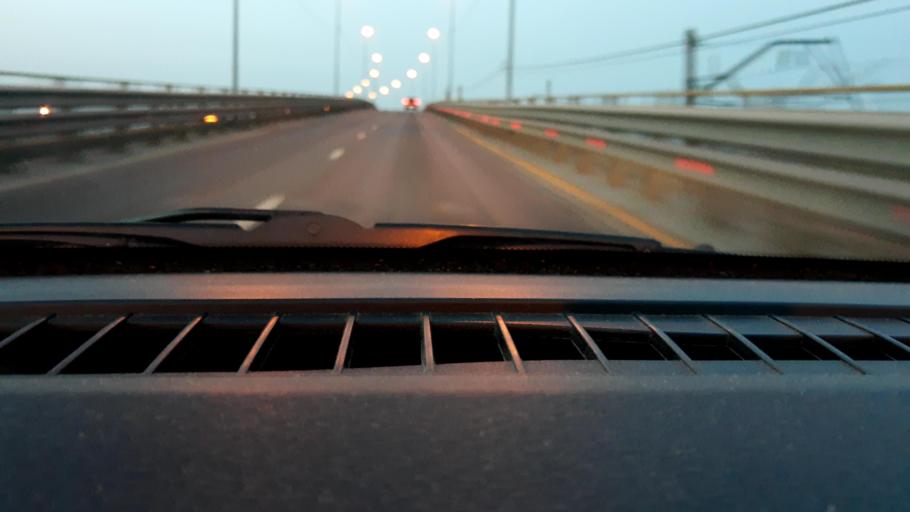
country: RU
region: Nizjnij Novgorod
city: Neklyudovo
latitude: 56.3625
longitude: 43.9323
